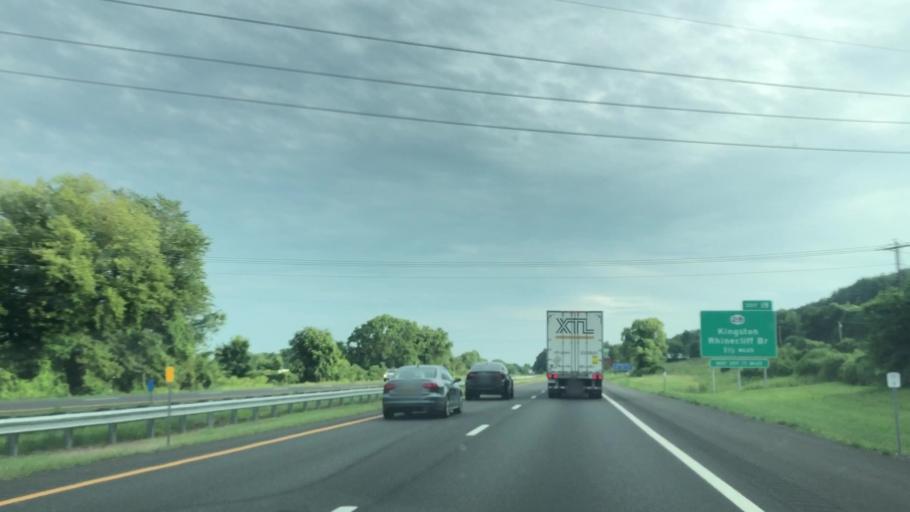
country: US
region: New York
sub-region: Ulster County
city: Lincoln Park
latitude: 41.9669
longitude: -74.0151
